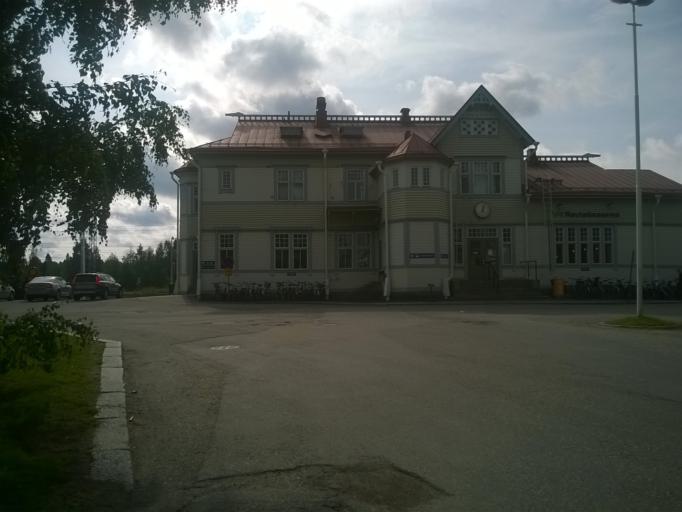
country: FI
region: Kainuu
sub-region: Kajaani
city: Kajaani
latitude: 64.2204
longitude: 27.7386
